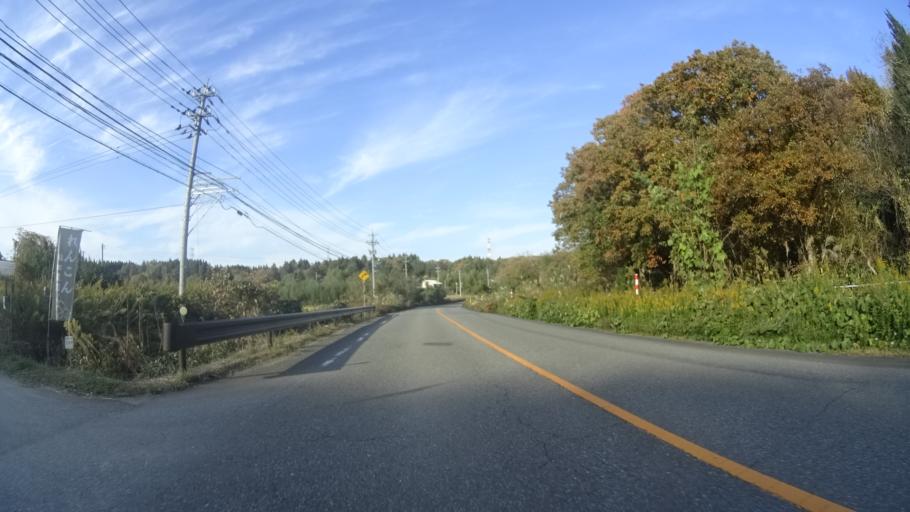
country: JP
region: Ishikawa
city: Hakui
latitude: 37.0549
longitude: 136.7764
